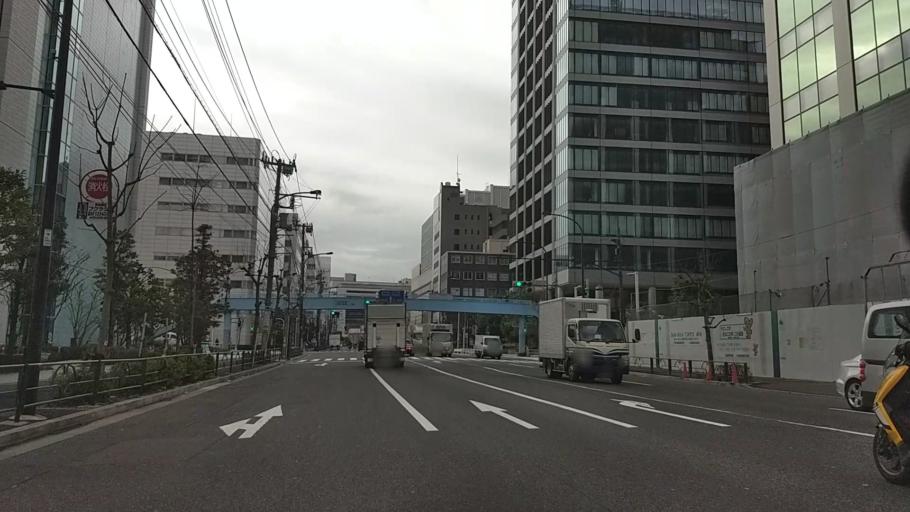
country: JP
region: Tokyo
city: Tokyo
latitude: 35.6301
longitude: 139.7451
